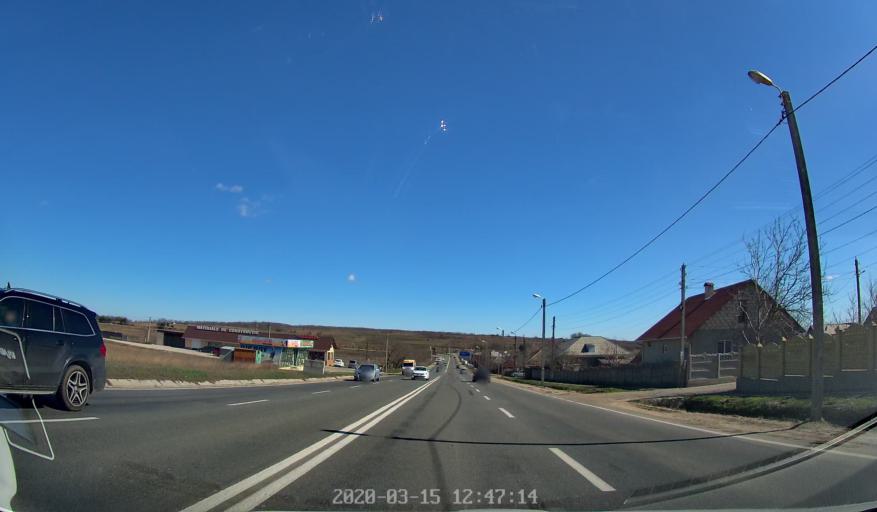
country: MD
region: Orhei
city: Orhei
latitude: 47.2644
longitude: 28.7759
